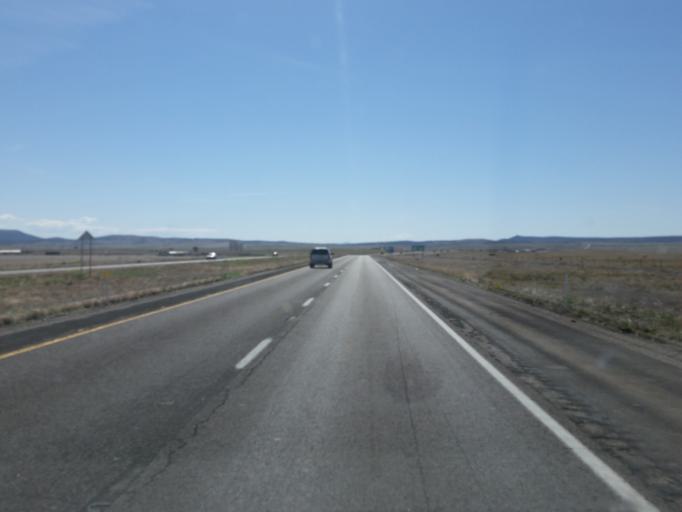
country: US
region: Arizona
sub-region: Mohave County
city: Peach Springs
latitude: 35.3168
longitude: -112.8759
